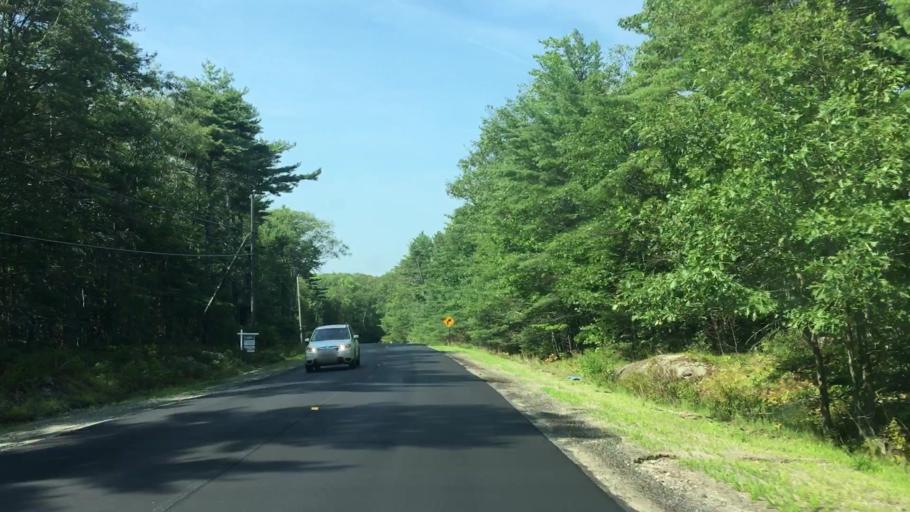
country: US
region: Maine
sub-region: Sagadahoc County
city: Woolwich
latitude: 43.9282
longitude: -69.8008
